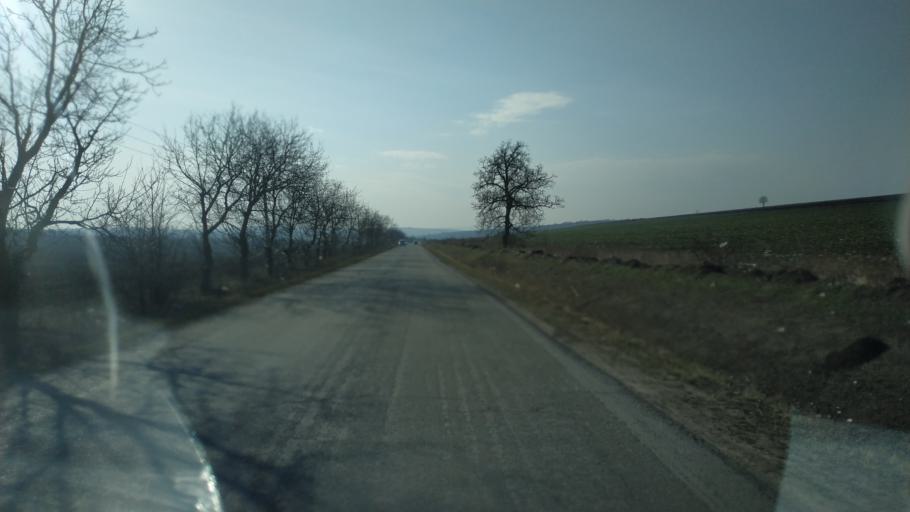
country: MD
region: Chisinau
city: Singera
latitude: 46.8533
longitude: 29.0221
